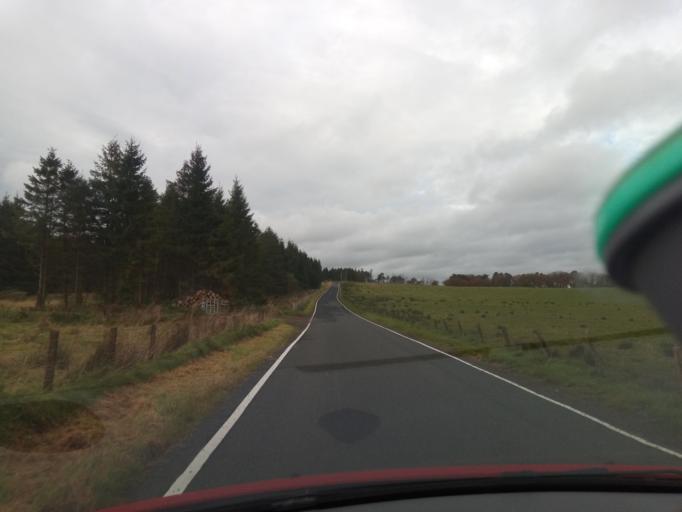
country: GB
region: Scotland
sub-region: West Lothian
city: West Calder
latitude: 55.8211
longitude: -3.5974
